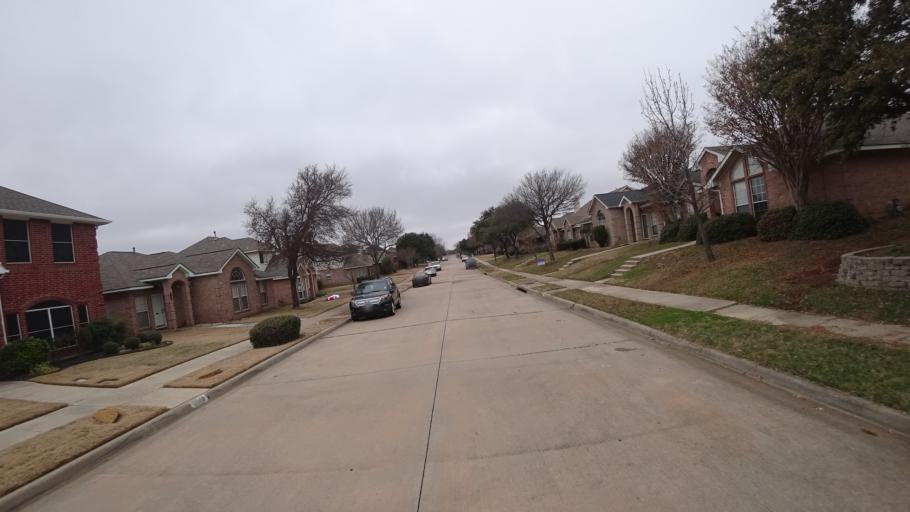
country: US
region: Texas
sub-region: Denton County
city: Lewisville
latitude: 33.0296
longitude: -97.0336
